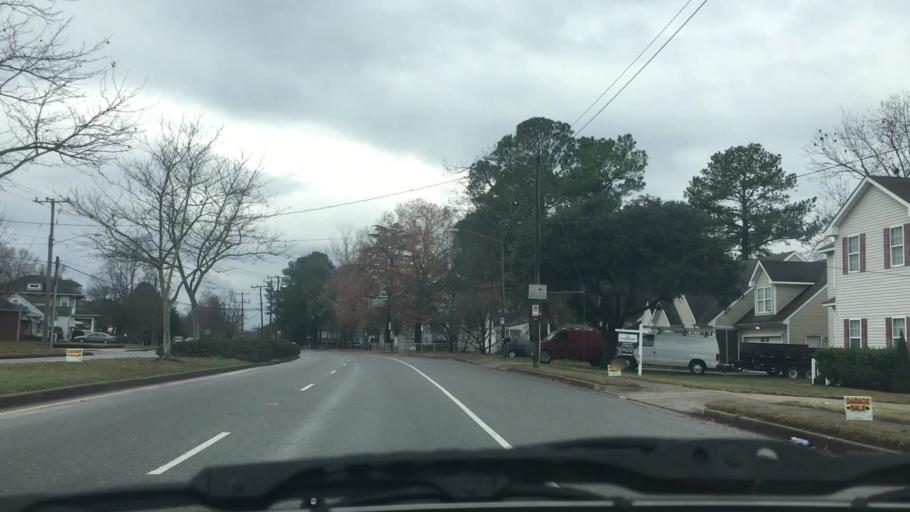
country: US
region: Virginia
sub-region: City of Norfolk
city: Norfolk
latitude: 36.8837
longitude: -76.2462
